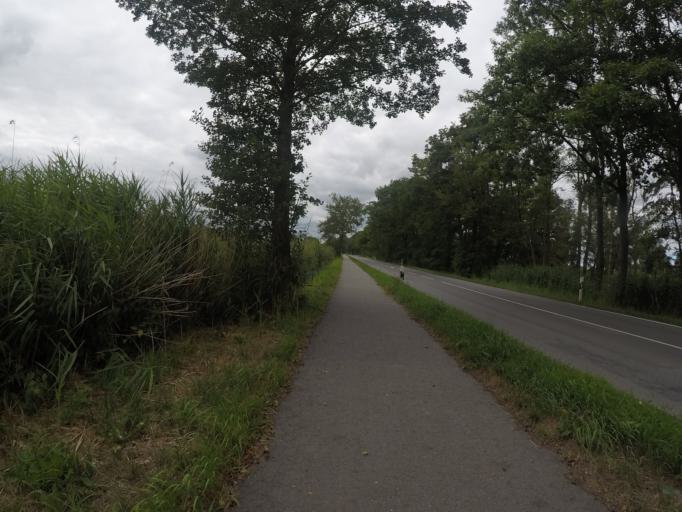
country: DE
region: Lower Saxony
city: Grossenworden
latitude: 53.6707
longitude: 9.2964
